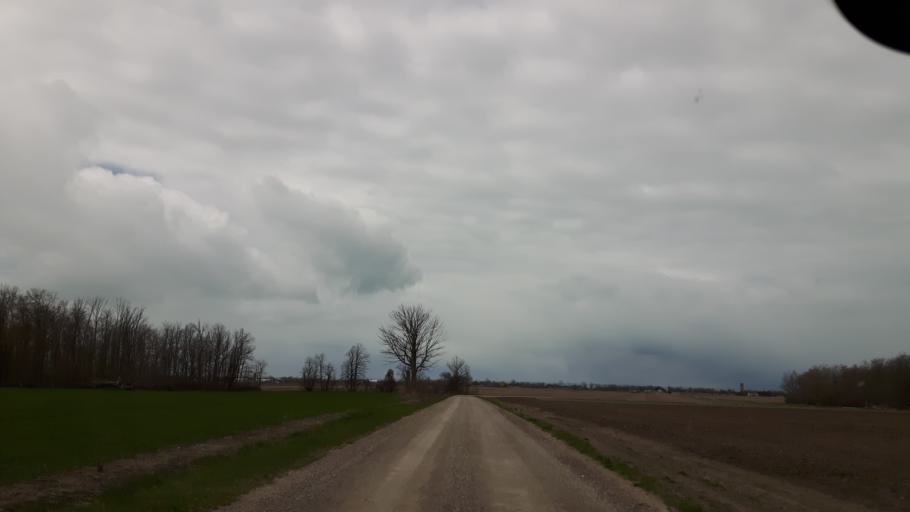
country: CA
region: Ontario
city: Bluewater
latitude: 43.4711
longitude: -81.6771
